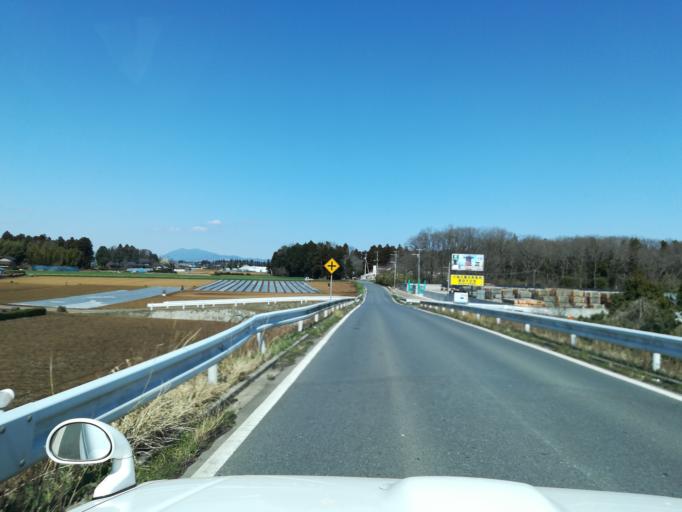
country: JP
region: Ibaraki
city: Ami
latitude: 35.9928
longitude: 140.1792
